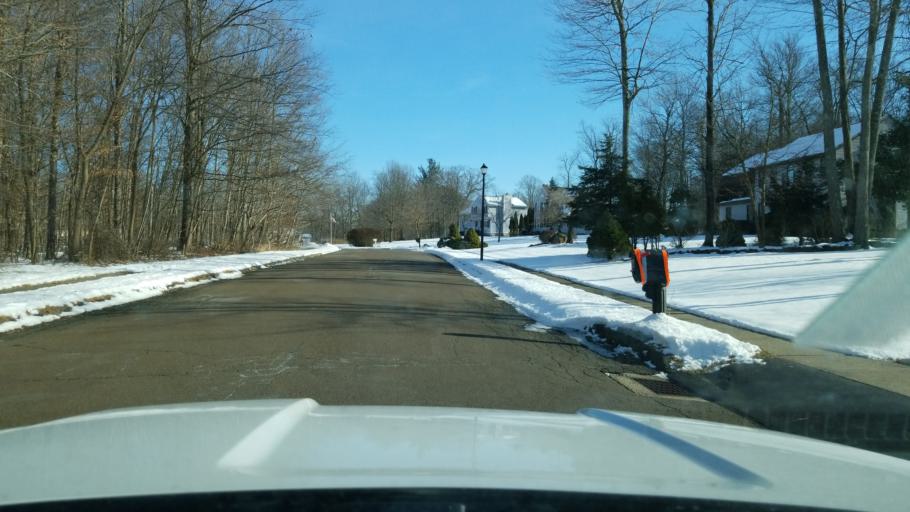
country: US
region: Connecticut
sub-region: New Haven County
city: Wallingford
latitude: 41.4854
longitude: -72.8577
